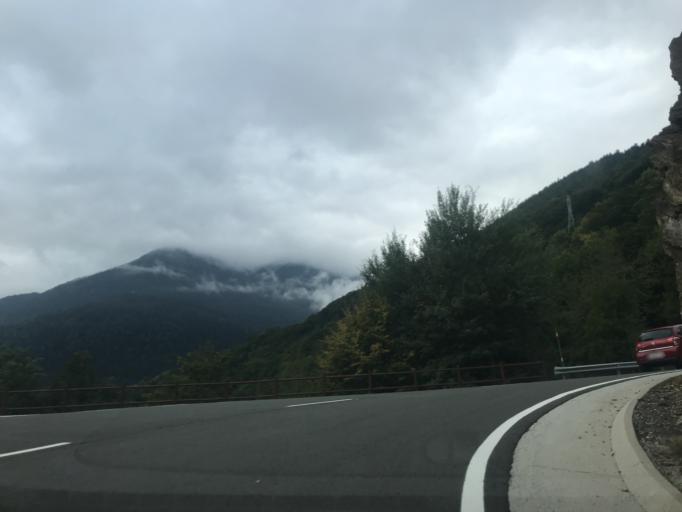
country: ES
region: Catalonia
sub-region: Provincia de Lleida
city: Les
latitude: 42.7782
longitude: 0.6803
